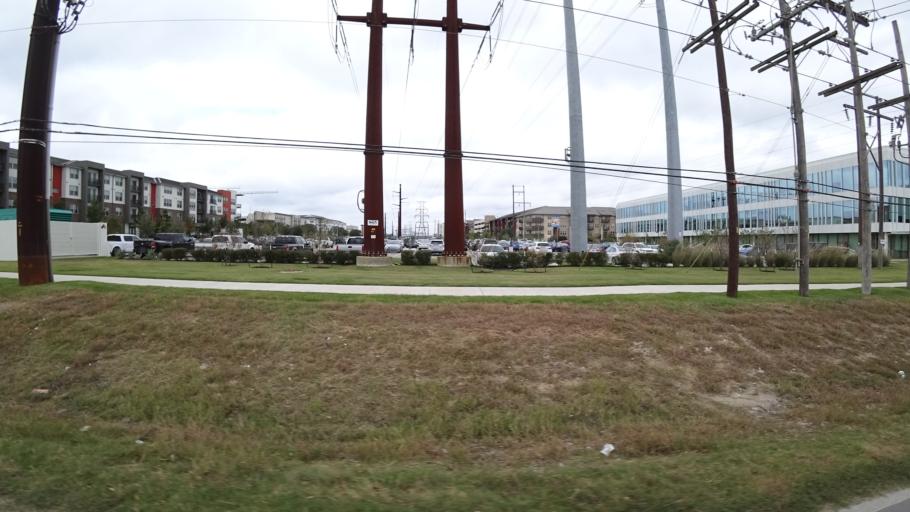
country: US
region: Texas
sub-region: Travis County
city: Wells Branch
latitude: 30.3973
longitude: -97.7198
